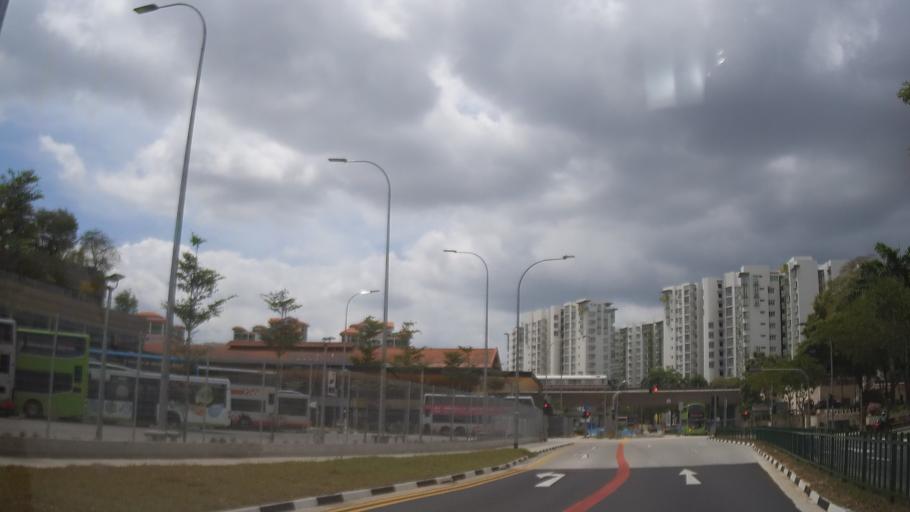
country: MY
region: Johor
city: Johor Bahru
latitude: 1.3863
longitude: 103.7456
